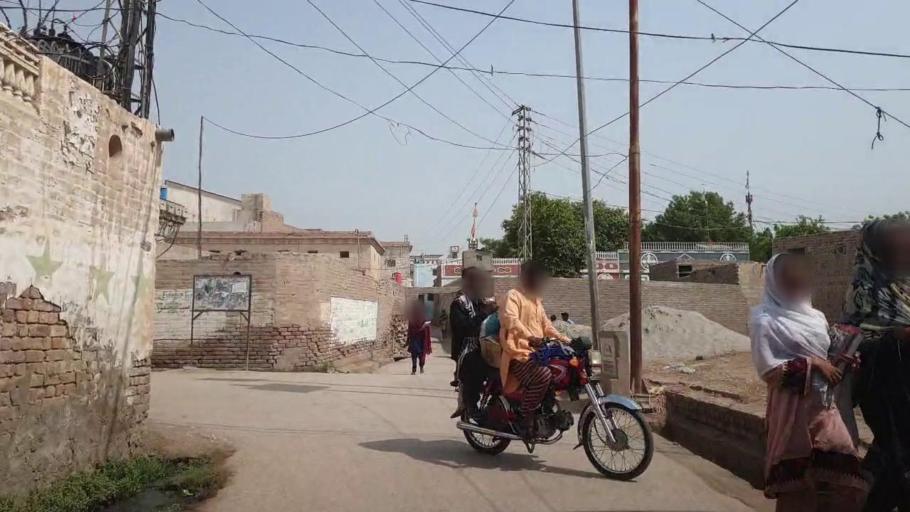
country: PK
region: Sindh
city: Gambat
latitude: 27.3778
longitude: 68.5155
